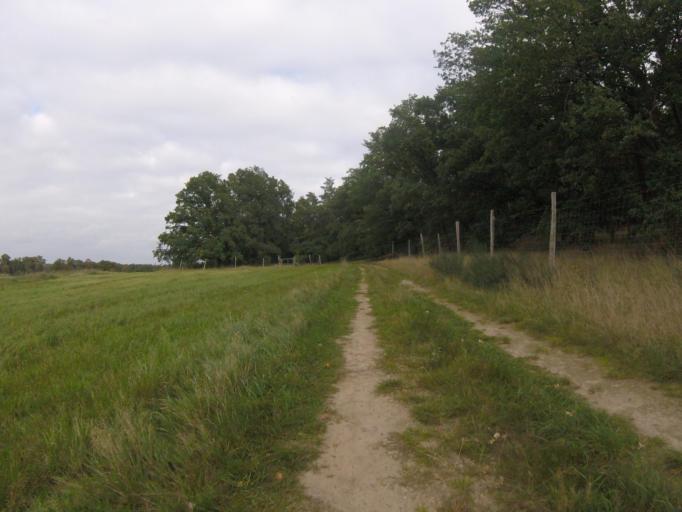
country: DE
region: Brandenburg
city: Mittenwalde
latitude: 52.2675
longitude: 13.4998
